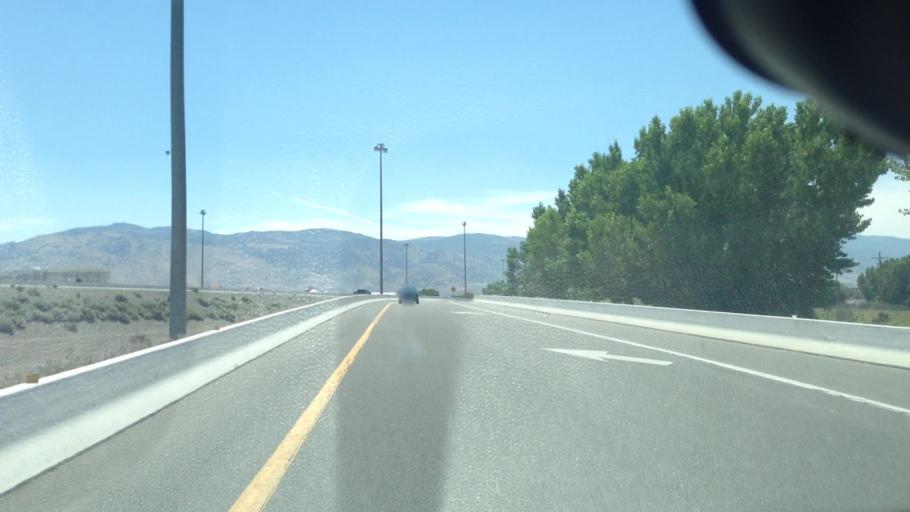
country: US
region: Nevada
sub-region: Washoe County
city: Sparks
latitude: 39.4382
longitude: -119.7663
